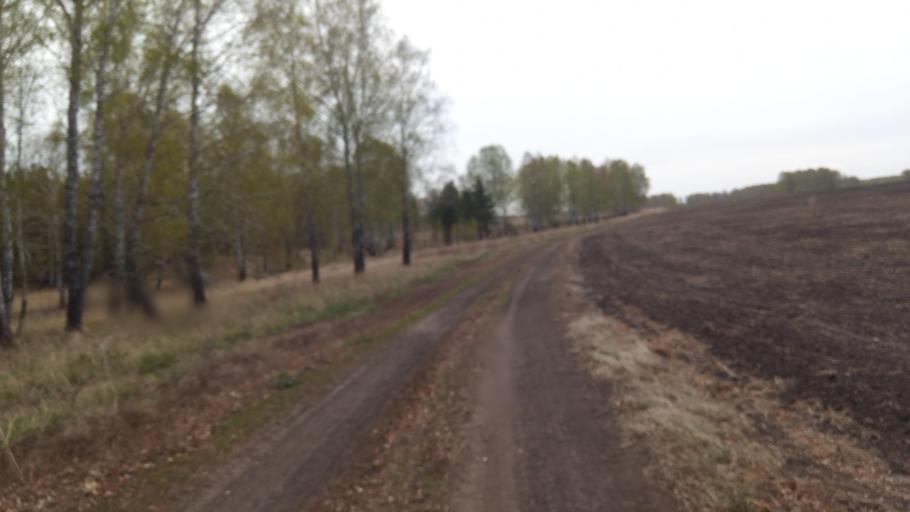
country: RU
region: Chelyabinsk
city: Timiryazevskiy
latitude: 55.0180
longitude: 60.8559
